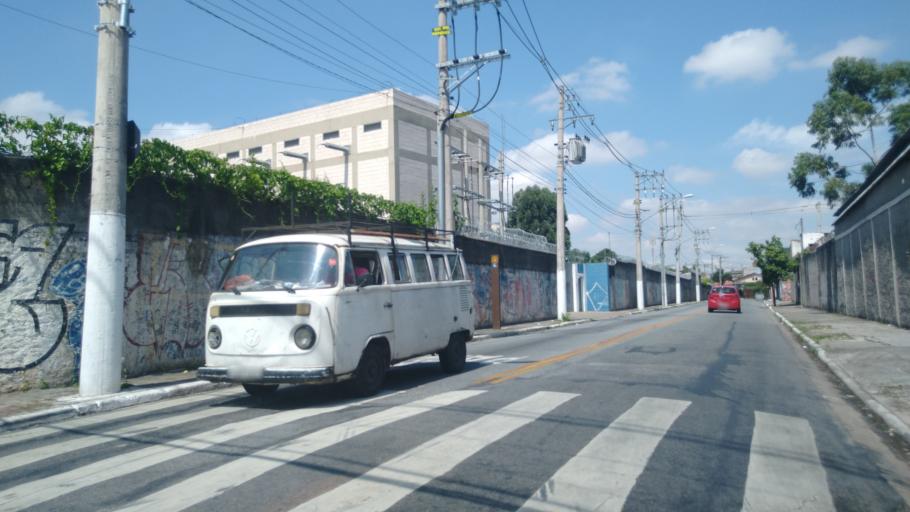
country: BR
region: Sao Paulo
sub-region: Guarulhos
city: Guarulhos
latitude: -23.4691
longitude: -46.5773
